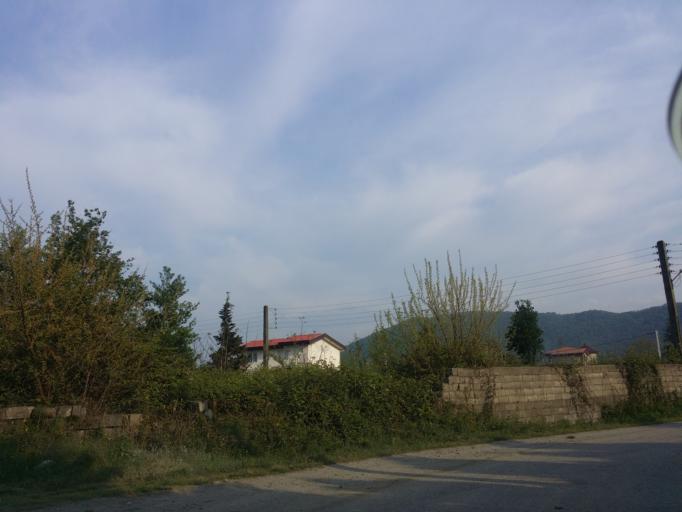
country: IR
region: Mazandaran
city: Chalus
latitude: 36.6615
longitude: 51.3662
